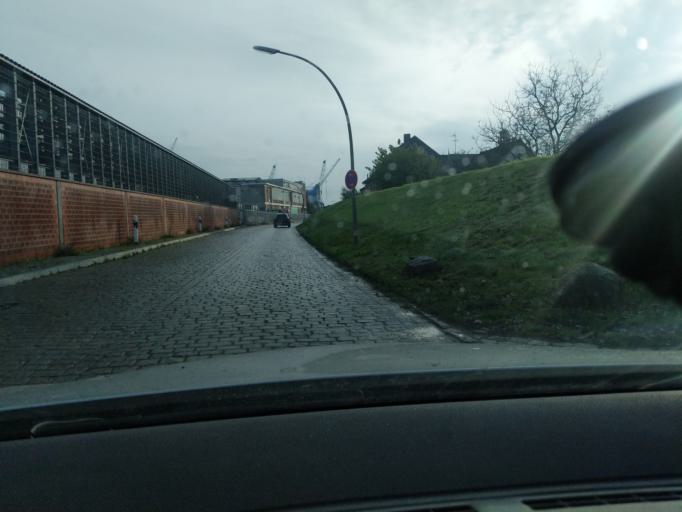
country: DE
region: Lower Saxony
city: Neu Wulmstorf
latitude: 53.5321
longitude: 9.7826
